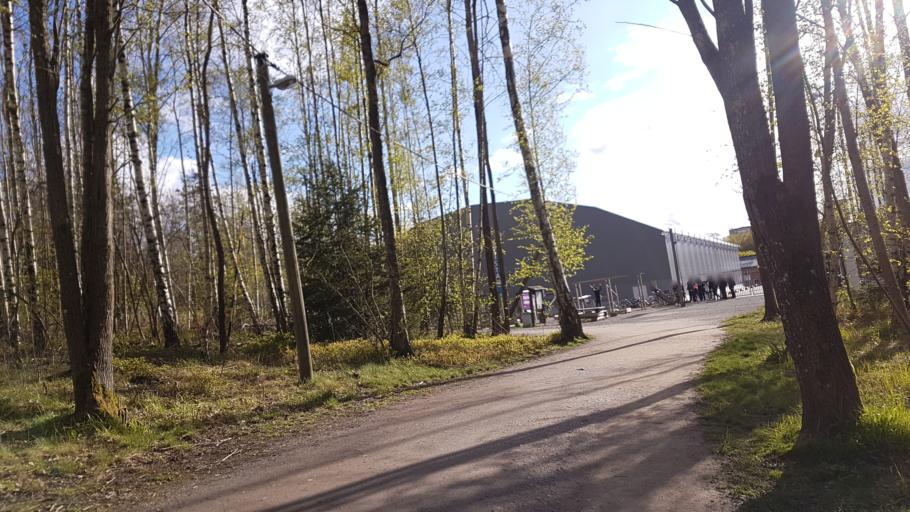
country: SE
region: Stockholm
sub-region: Nacka Kommun
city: Nacka
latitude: 59.2861
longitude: 18.1262
